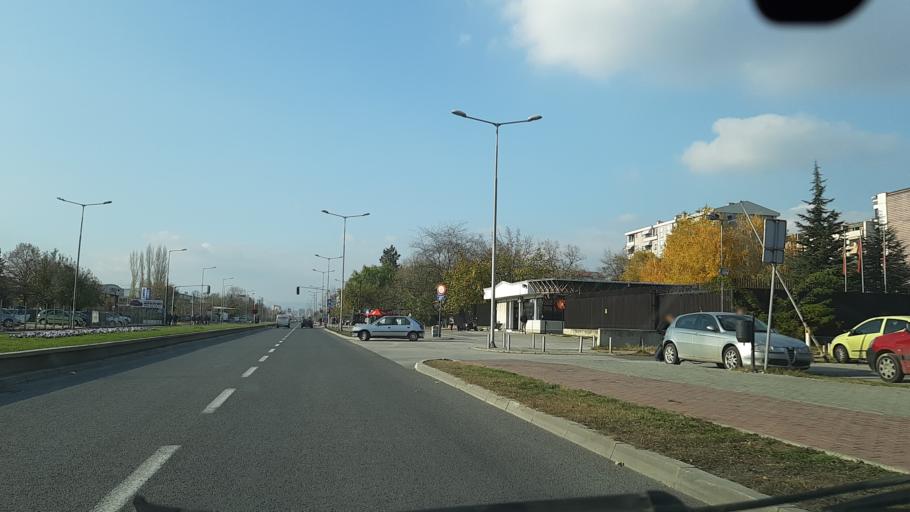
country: MK
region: Kisela Voda
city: Usje
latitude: 41.9780
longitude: 21.4631
